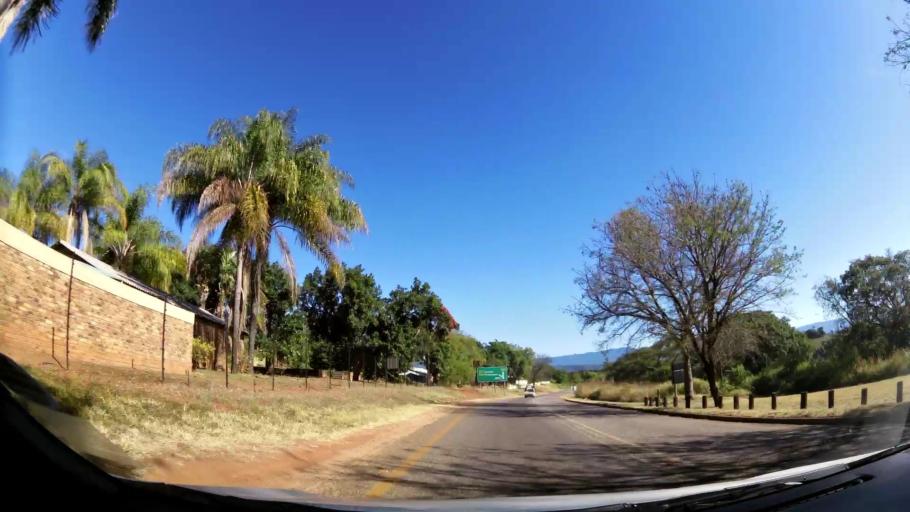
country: ZA
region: Limpopo
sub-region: Mopani District Municipality
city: Tzaneen
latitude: -23.8427
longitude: 30.1449
